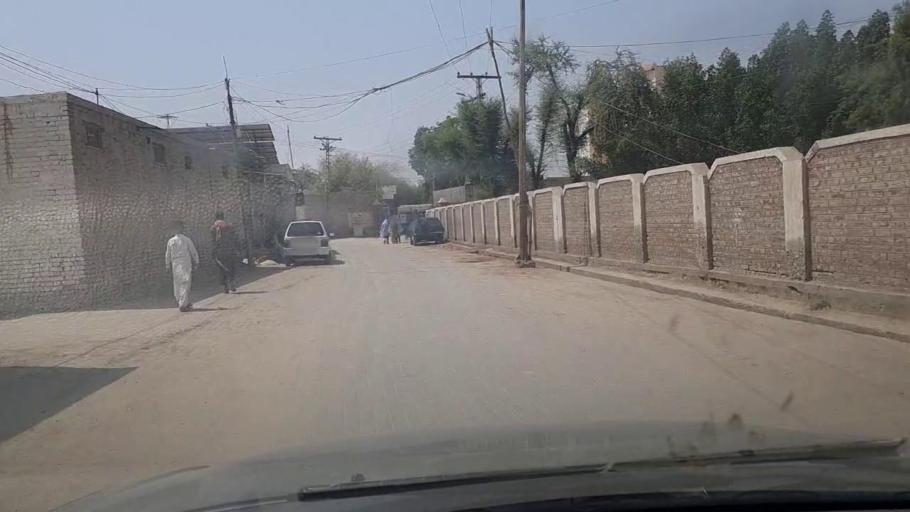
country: PK
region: Sindh
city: Adilpur
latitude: 27.9385
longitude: 69.3175
